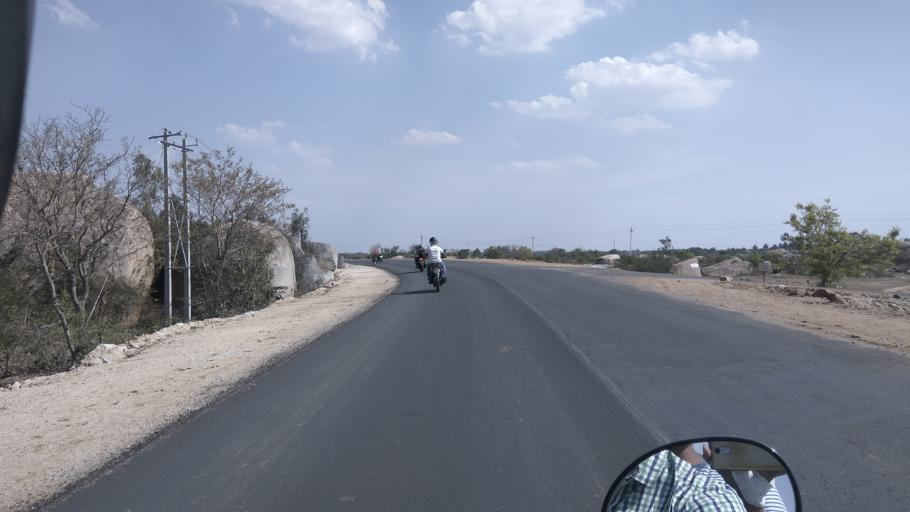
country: IN
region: Karnataka
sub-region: Kolar
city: Mulbagal
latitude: 13.1762
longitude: 78.3539
